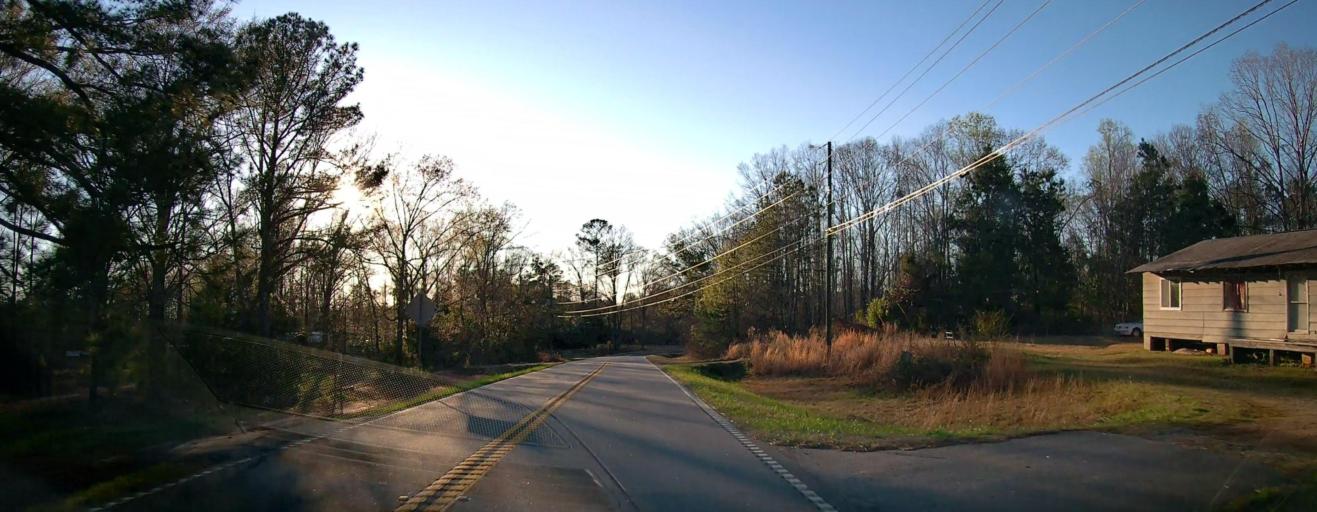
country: US
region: Georgia
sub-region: Harris County
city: Hamilton
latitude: 32.6232
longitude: -84.8174
